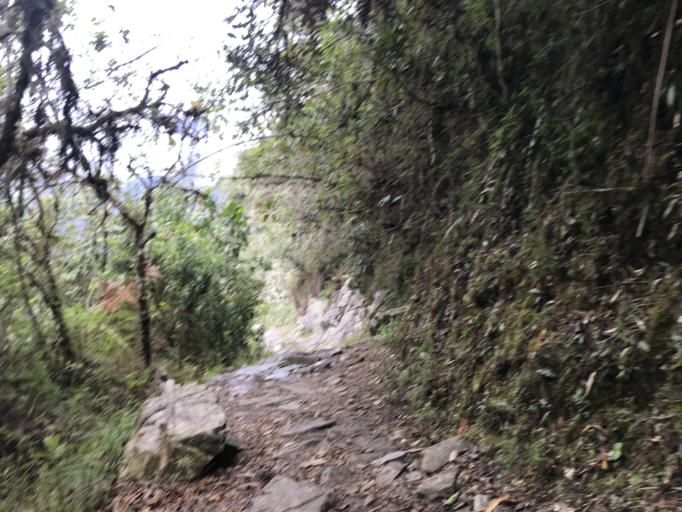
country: PE
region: Cusco
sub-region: Provincia de La Convencion
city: Santa Teresa
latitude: -13.1717
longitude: -72.5336
